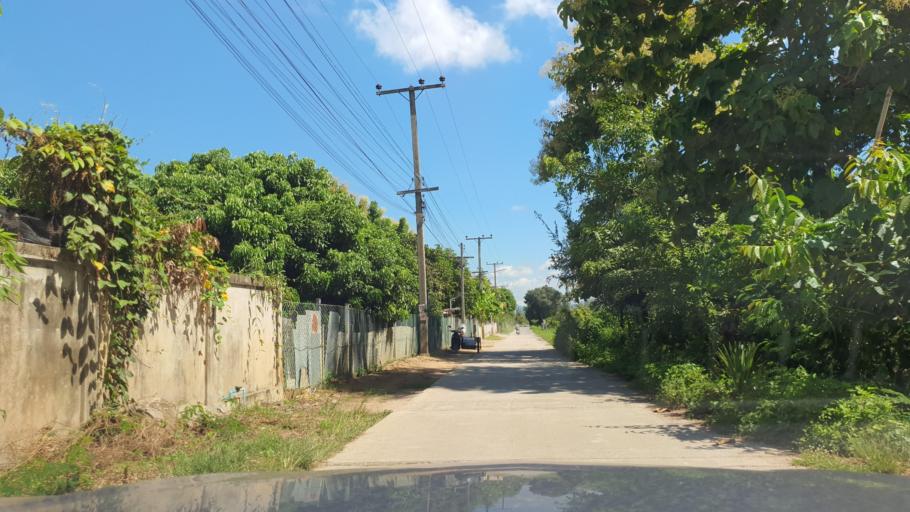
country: TH
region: Chiang Mai
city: San Kamphaeng
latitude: 18.7662
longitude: 99.1696
